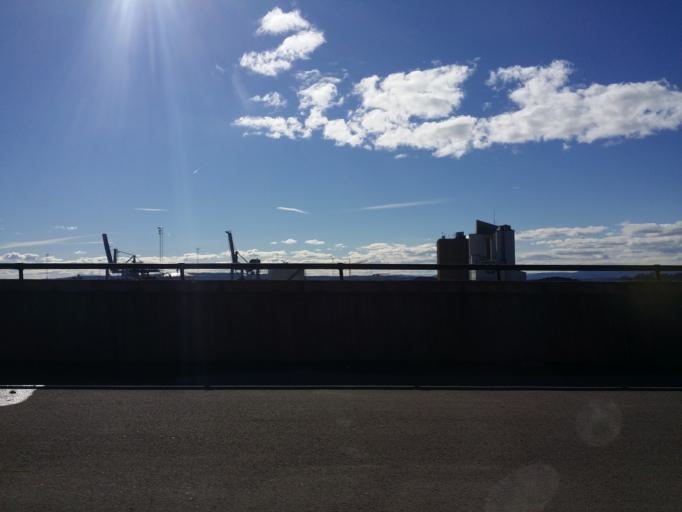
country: NO
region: Oslo
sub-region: Oslo
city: Oslo
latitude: 59.8905
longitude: 10.7623
